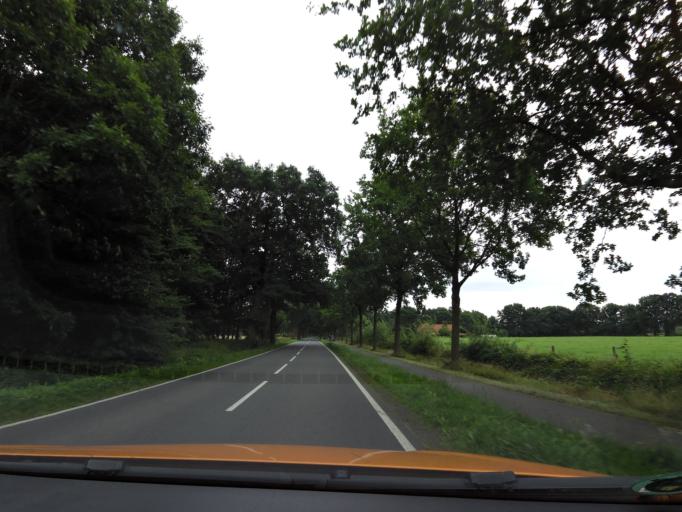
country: DE
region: Lower Saxony
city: Wiefelstede
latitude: 53.2027
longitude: 8.1193
